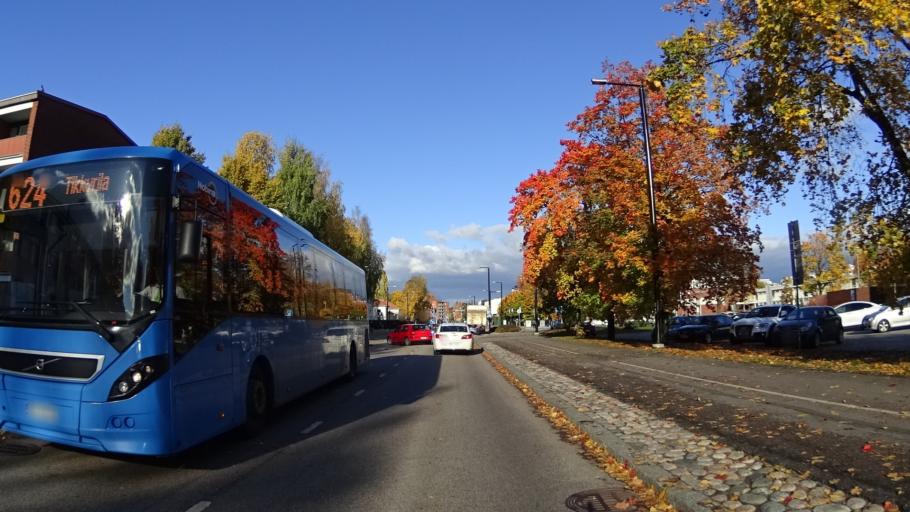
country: FI
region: Uusimaa
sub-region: Helsinki
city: Vantaa
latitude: 60.2953
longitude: 25.0389
